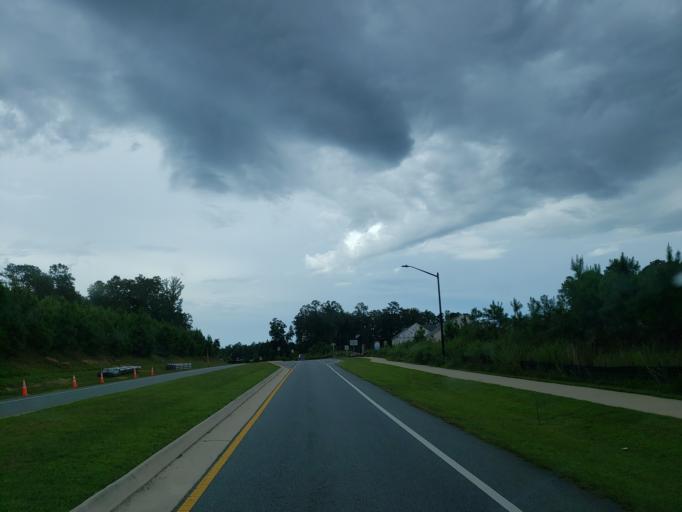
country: US
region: Georgia
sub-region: Cobb County
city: Acworth
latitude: 34.0297
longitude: -84.7608
